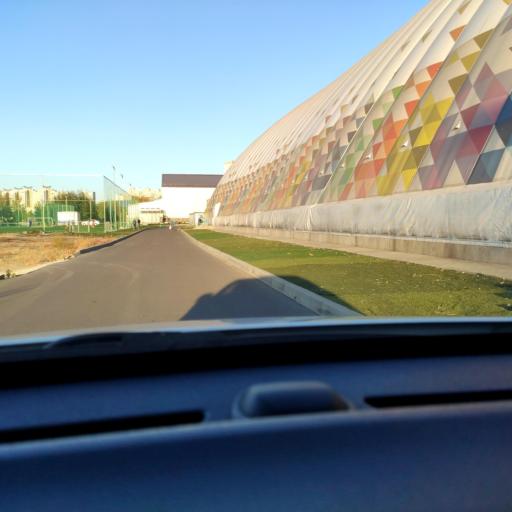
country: RU
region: Voronezj
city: Voronezh
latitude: 51.6734
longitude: 39.2367
